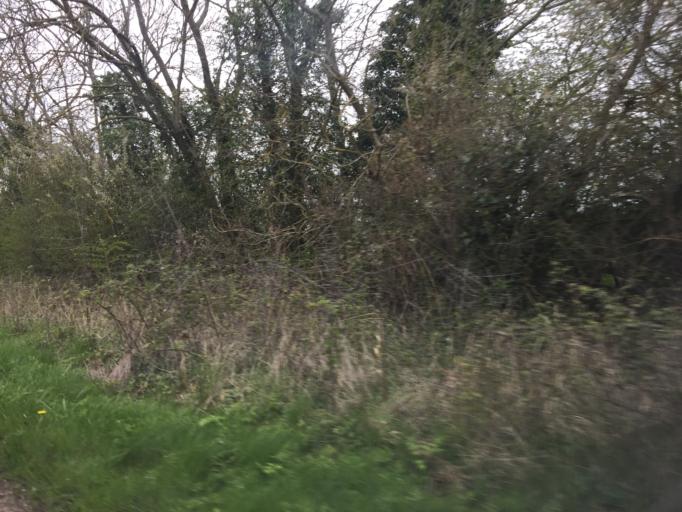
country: GB
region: England
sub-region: Oxfordshire
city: Bicester
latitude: 51.9286
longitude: -1.1461
